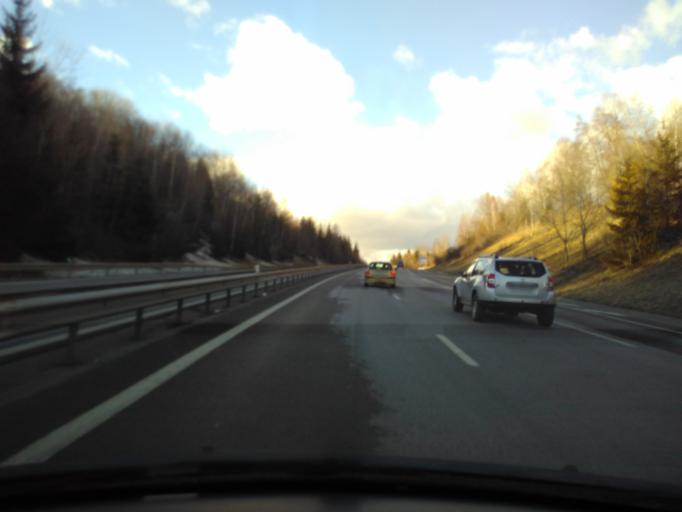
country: FR
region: Rhone-Alpes
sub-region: Departement de la Haute-Savoie
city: Groisy
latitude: 45.9980
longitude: 6.1508
